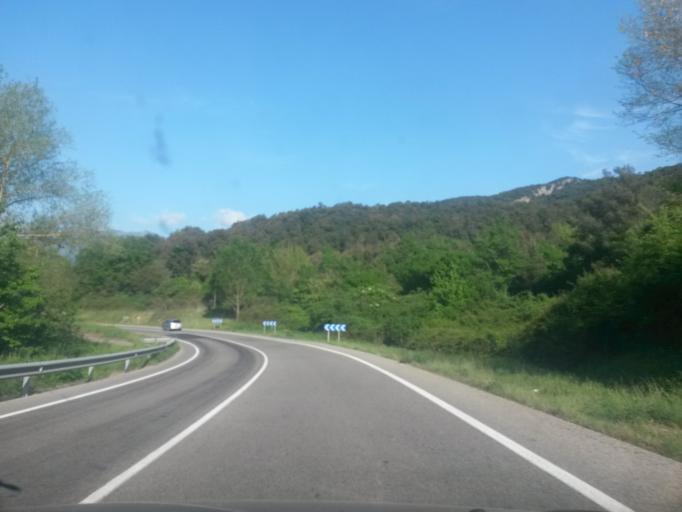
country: ES
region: Catalonia
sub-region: Provincia de Girona
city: Bas
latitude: 42.1236
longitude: 2.4840
